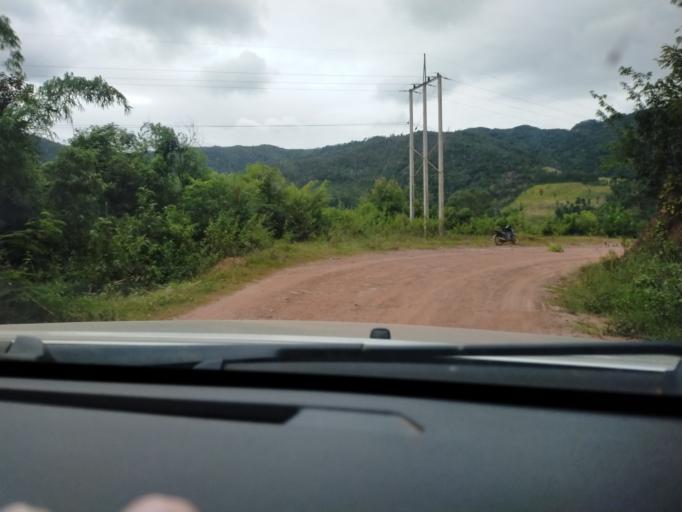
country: TH
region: Nan
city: Chaloem Phra Kiat
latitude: 19.7638
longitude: 101.3484
